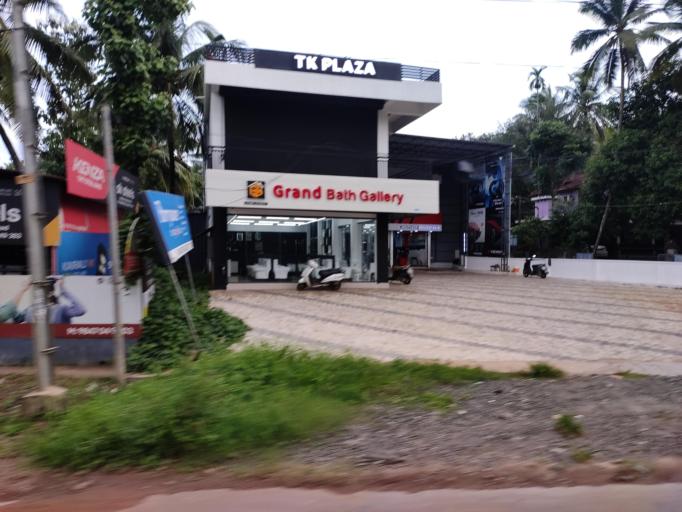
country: IN
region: Kerala
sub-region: Palakkad district
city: Mannarakkat
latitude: 10.9890
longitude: 76.4766
